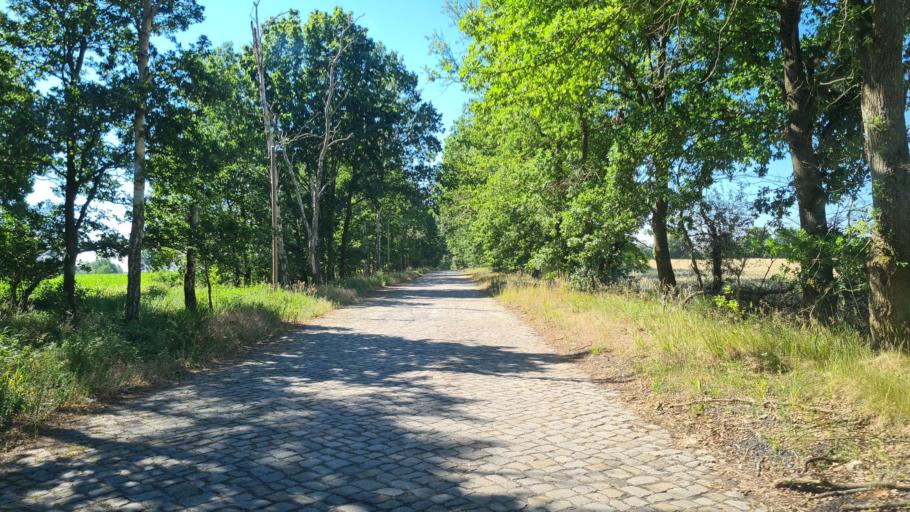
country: DE
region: Brandenburg
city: Niedergorsdorf
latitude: 52.0034
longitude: 12.9648
